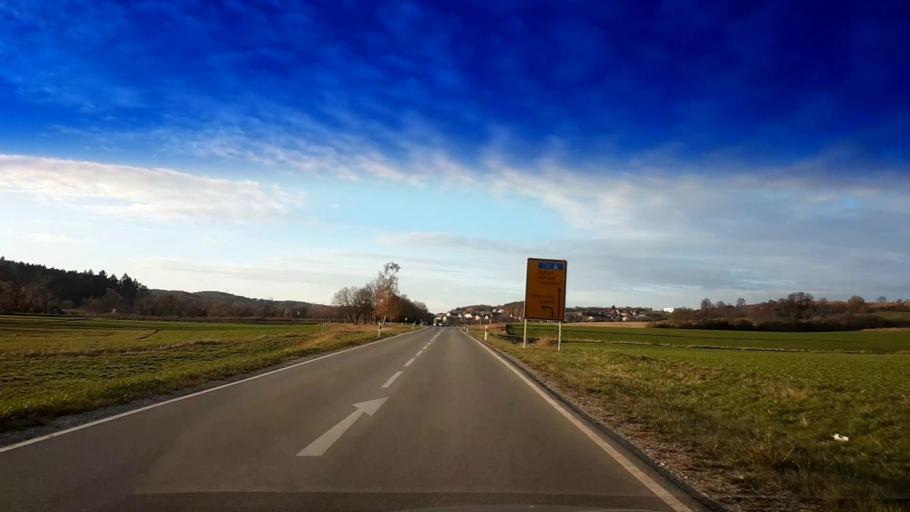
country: DE
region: Bavaria
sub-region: Upper Franconia
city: Priesendorf
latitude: 49.8889
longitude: 10.7411
